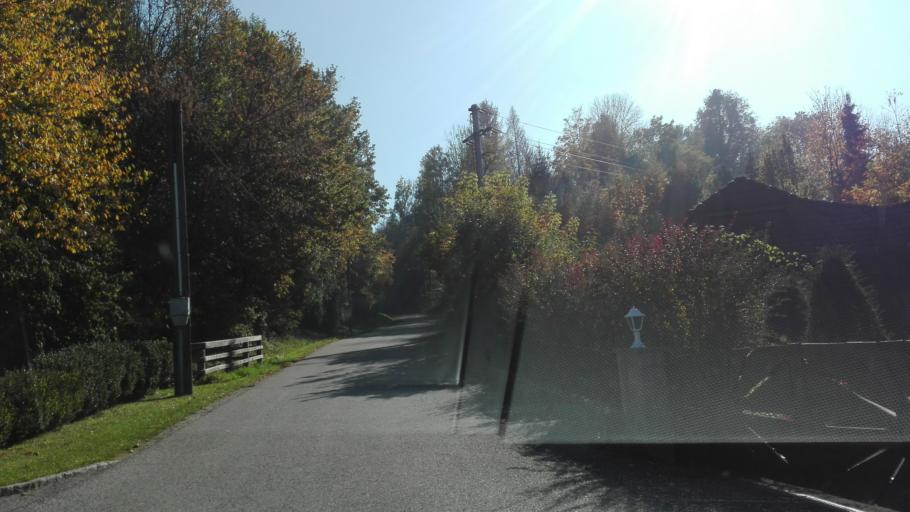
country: AT
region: Upper Austria
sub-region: Politischer Bezirk Urfahr-Umgebung
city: Ottensheim
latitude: 48.3076
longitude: 14.1759
